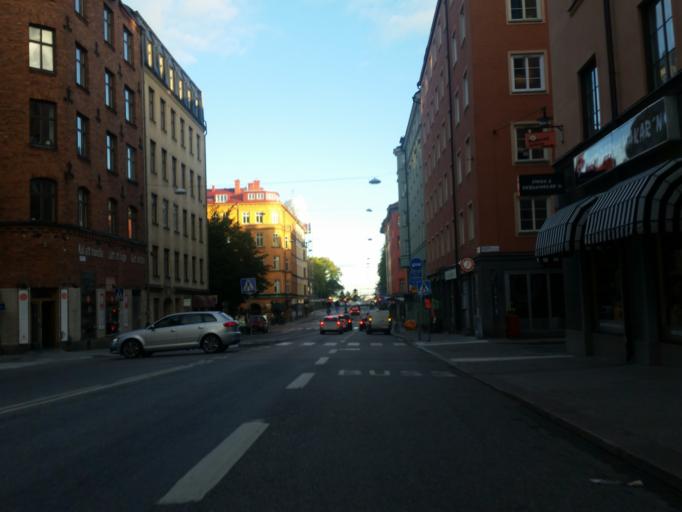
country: SE
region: Stockholm
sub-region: Stockholms Kommun
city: OEstermalm
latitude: 59.3146
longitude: 18.0843
